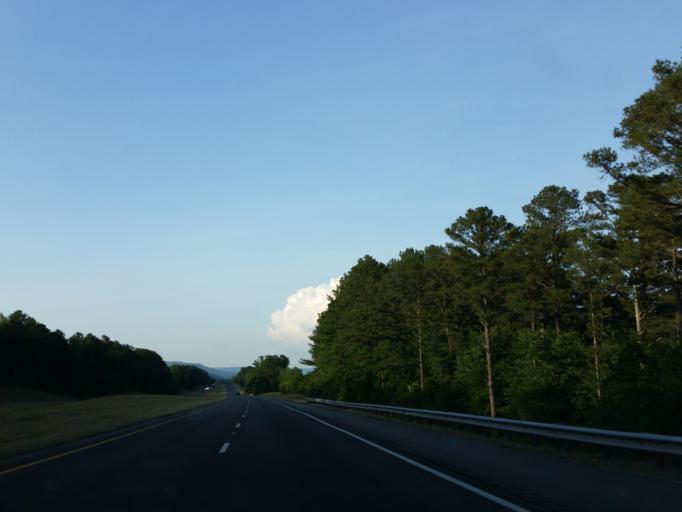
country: US
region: Alabama
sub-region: DeKalb County
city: Henagar
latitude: 34.6292
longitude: -85.6228
